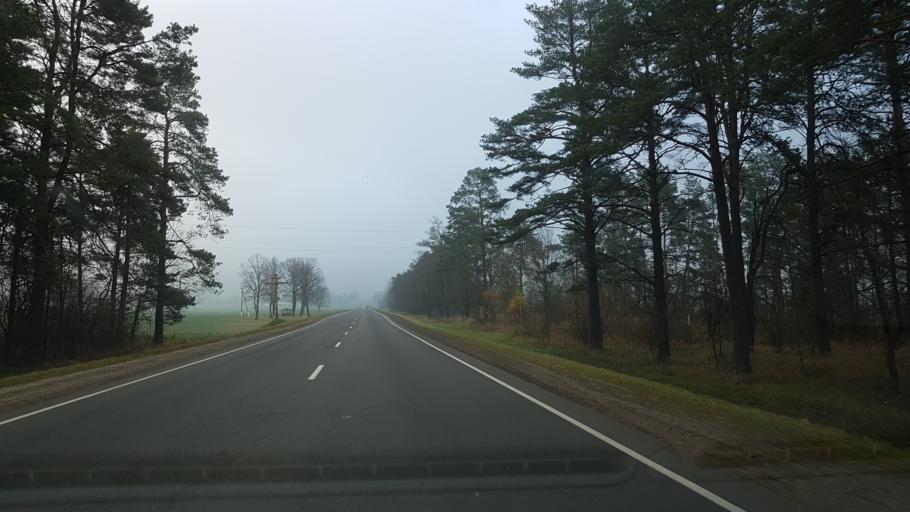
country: BY
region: Mogilev
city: Babruysk
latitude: 53.1672
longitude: 29.3317
